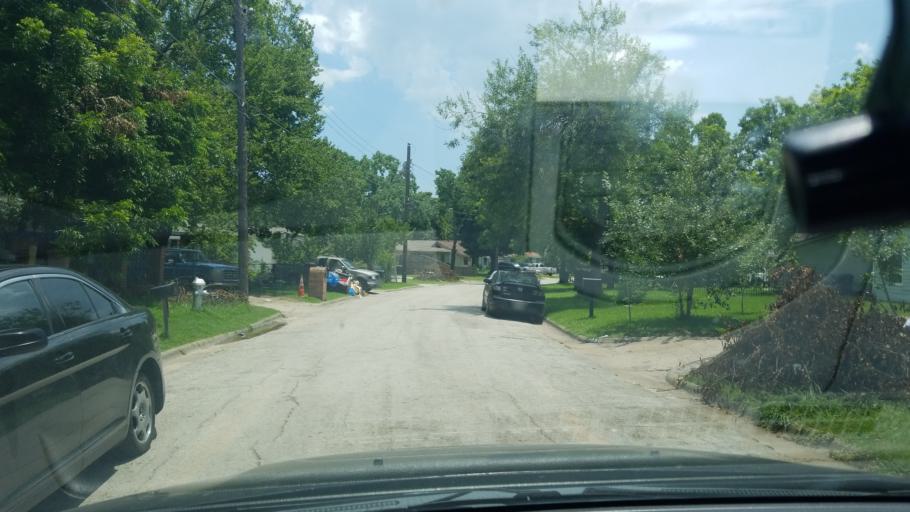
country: US
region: Texas
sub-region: Dallas County
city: Balch Springs
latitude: 32.7310
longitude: -96.6637
